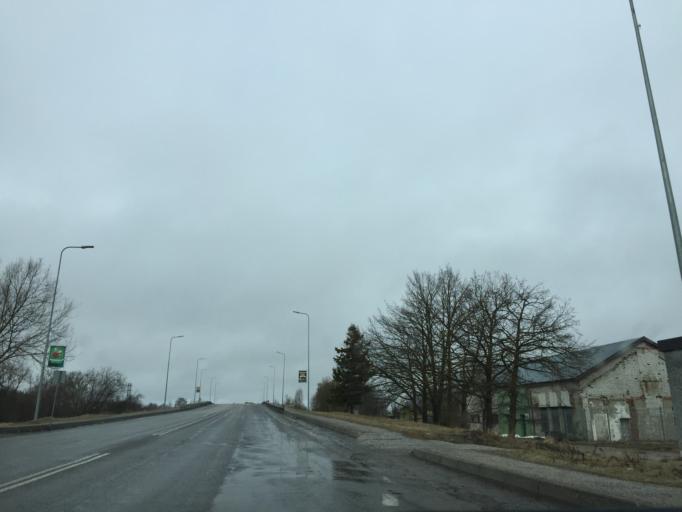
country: EE
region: Laeaene
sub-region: Haapsalu linn
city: Haapsalu
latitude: 58.9288
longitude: 23.5443
